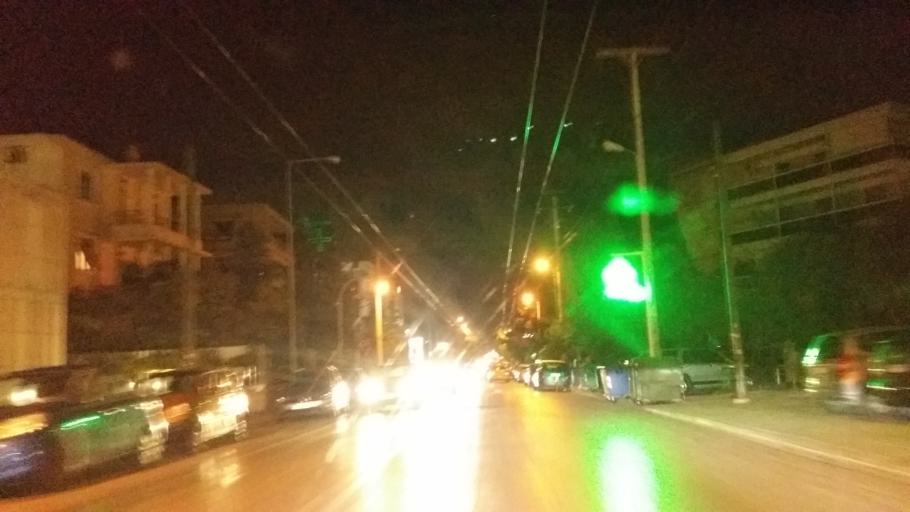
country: GR
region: Attica
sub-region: Nomarchia Athinas
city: Neo Psychiko
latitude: 38.0125
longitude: 23.7868
